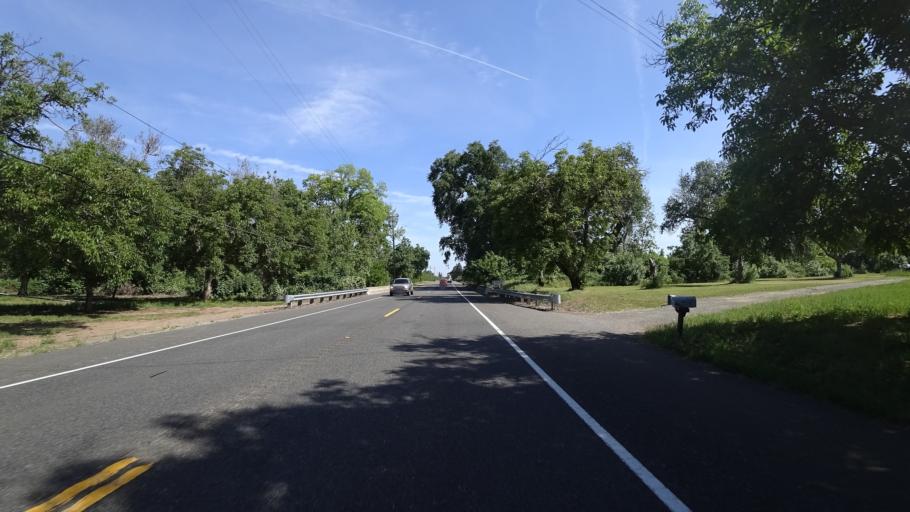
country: US
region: California
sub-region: Tehama County
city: Red Bluff
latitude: 40.1646
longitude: -122.1540
